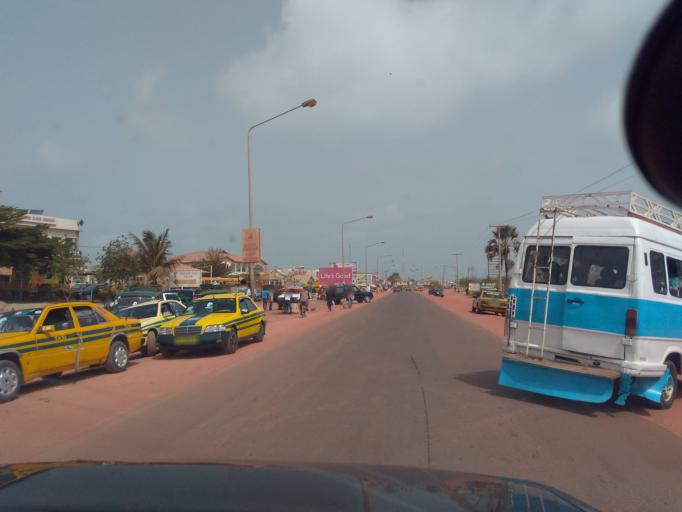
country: GM
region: Western
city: Sukuta
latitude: 13.4059
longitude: -16.7267
